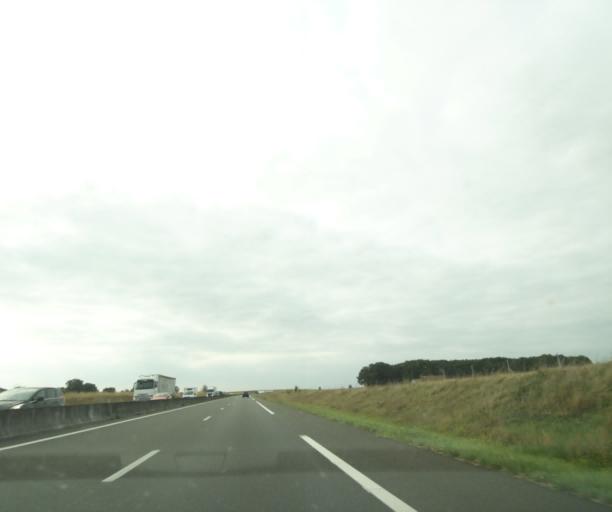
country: FR
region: Centre
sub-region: Departement d'Indre-et-Loire
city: Neuille-Pont-Pierre
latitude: 47.5944
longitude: 0.5459
